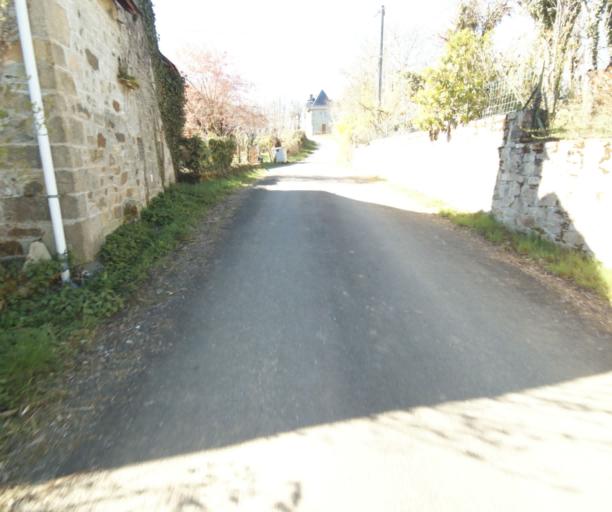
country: FR
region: Limousin
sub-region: Departement de la Correze
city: Chamboulive
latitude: 45.4122
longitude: 1.6986
